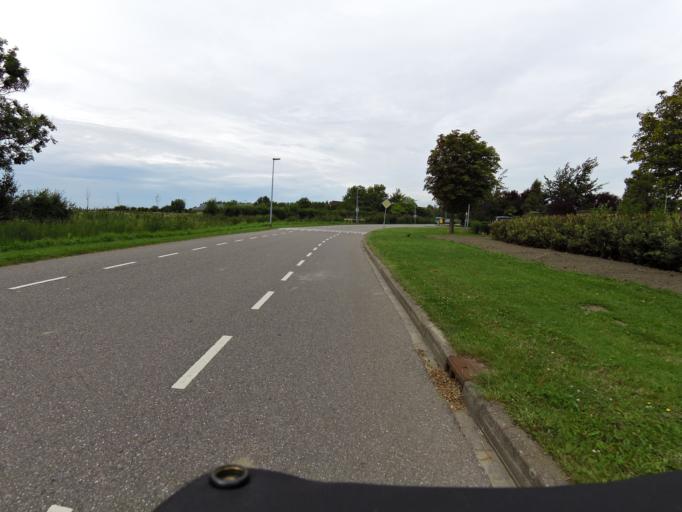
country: NL
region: South Holland
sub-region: Gemeente Goeree-Overflakkee
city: Middelharnis
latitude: 51.6930
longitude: 4.2037
